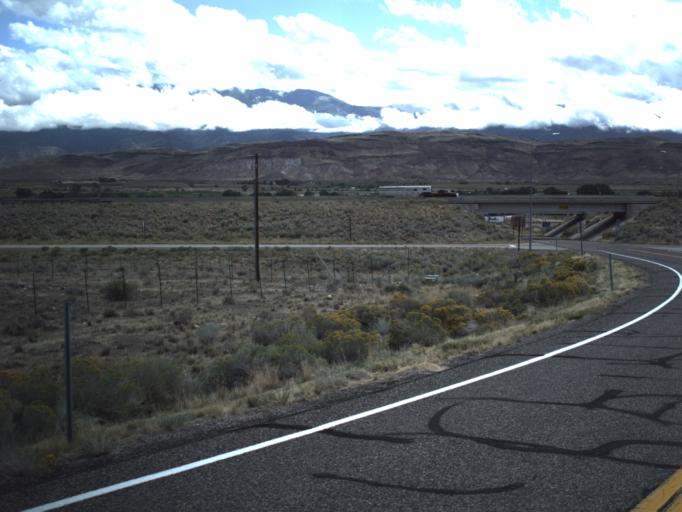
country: US
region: Utah
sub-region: Sevier County
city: Monroe
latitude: 38.6257
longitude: -112.2284
